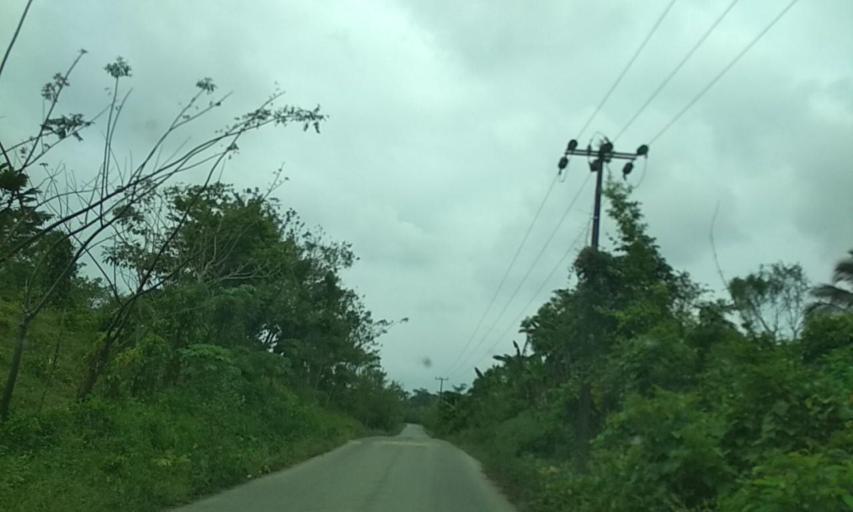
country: MX
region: Veracruz
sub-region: Uxpanapa
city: Poblado 10
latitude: 17.4688
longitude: -94.1144
